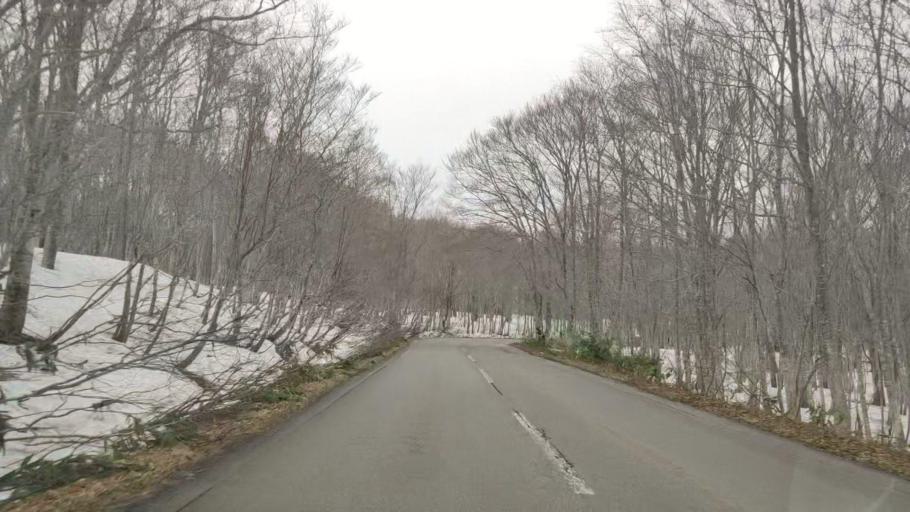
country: JP
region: Aomori
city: Aomori Shi
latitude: 40.6454
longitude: 140.9436
